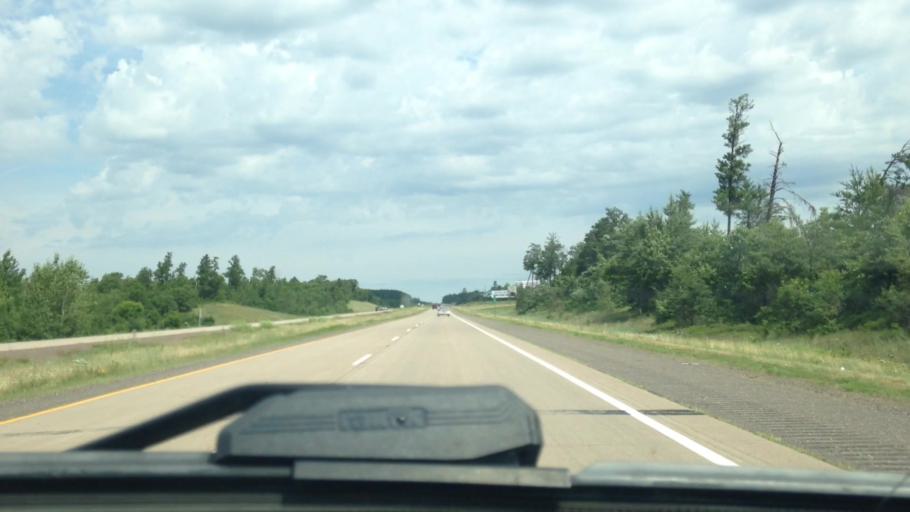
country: US
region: Wisconsin
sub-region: Douglas County
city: Lake Nebagamon
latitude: 46.1917
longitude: -91.7991
